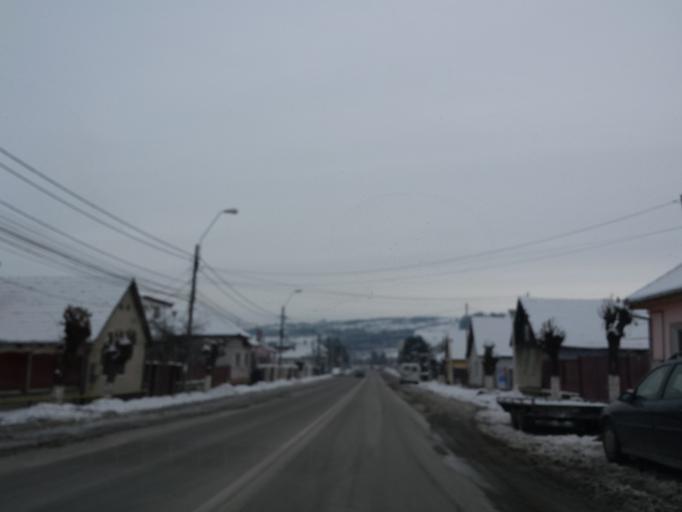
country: RO
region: Hunedoara
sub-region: Municipiul Deva
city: Deva
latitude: 45.8633
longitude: 22.9171
